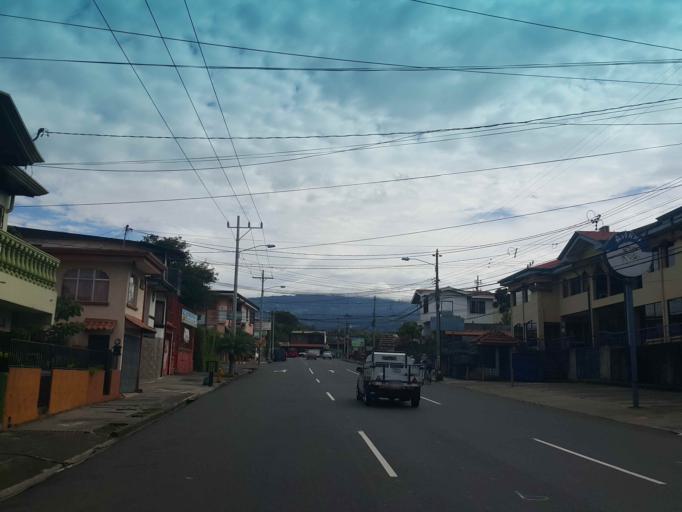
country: CR
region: Heredia
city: Heredia
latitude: 10.0028
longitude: -84.1125
